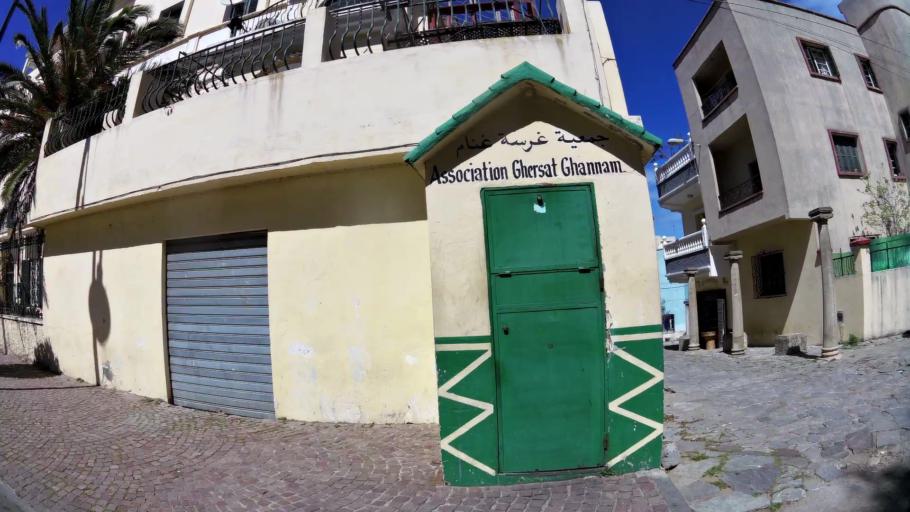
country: MA
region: Tanger-Tetouan
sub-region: Tanger-Assilah
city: Tangier
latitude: 35.7899
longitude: -5.8207
